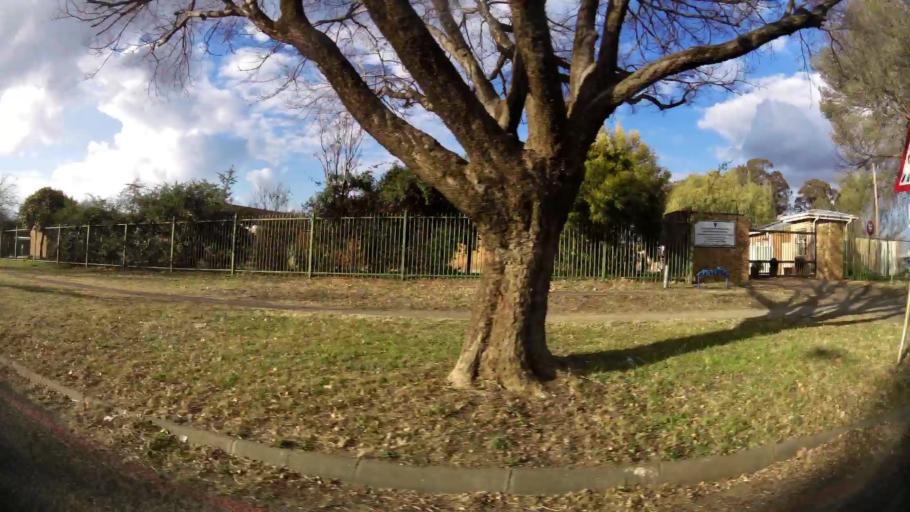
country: ZA
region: Orange Free State
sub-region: Mangaung Metropolitan Municipality
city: Bloemfontein
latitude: -29.1048
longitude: 26.1993
